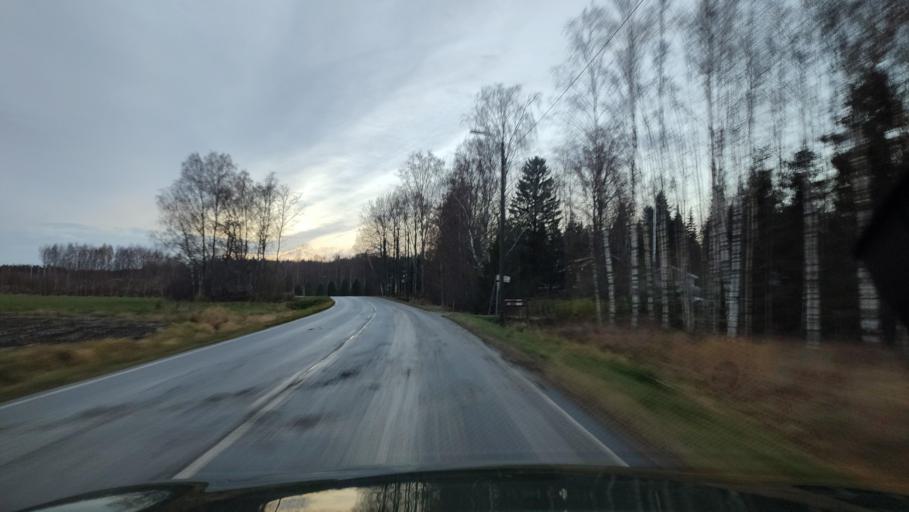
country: FI
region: Ostrobothnia
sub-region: Vaasa
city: Ristinummi
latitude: 63.0477
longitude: 21.7407
